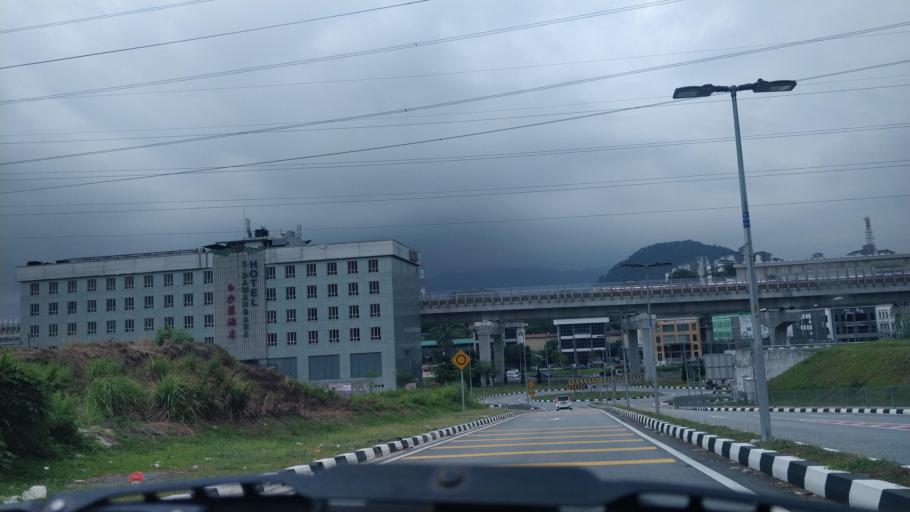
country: MY
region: Selangor
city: Kuang
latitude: 3.1965
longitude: 101.6067
